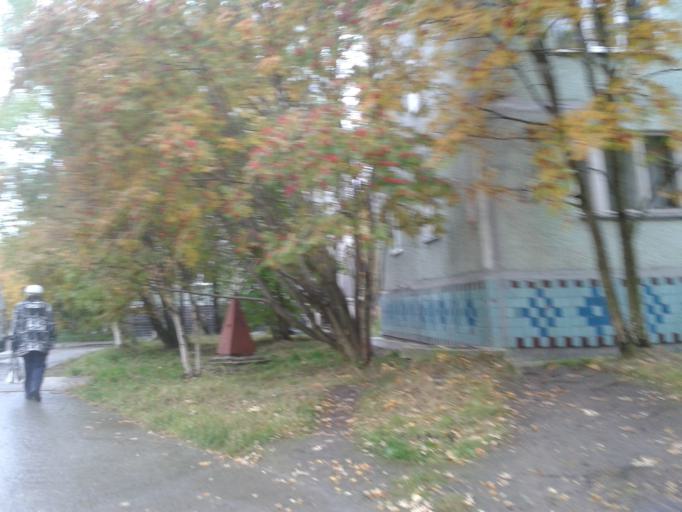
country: RU
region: Murmansk
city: Polyarnyye Zori
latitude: 67.3720
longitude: 32.4993
